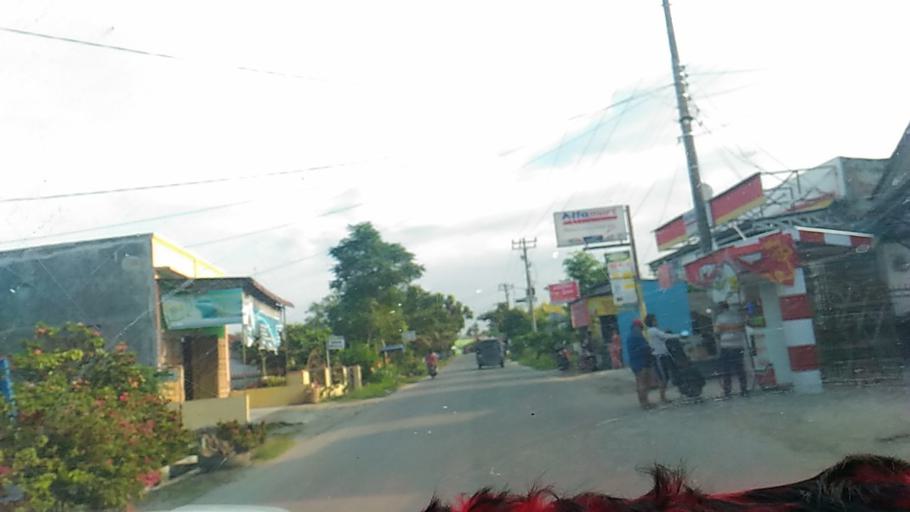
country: ID
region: North Sumatra
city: Labuhan Deli
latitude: 3.7057
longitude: 98.6001
